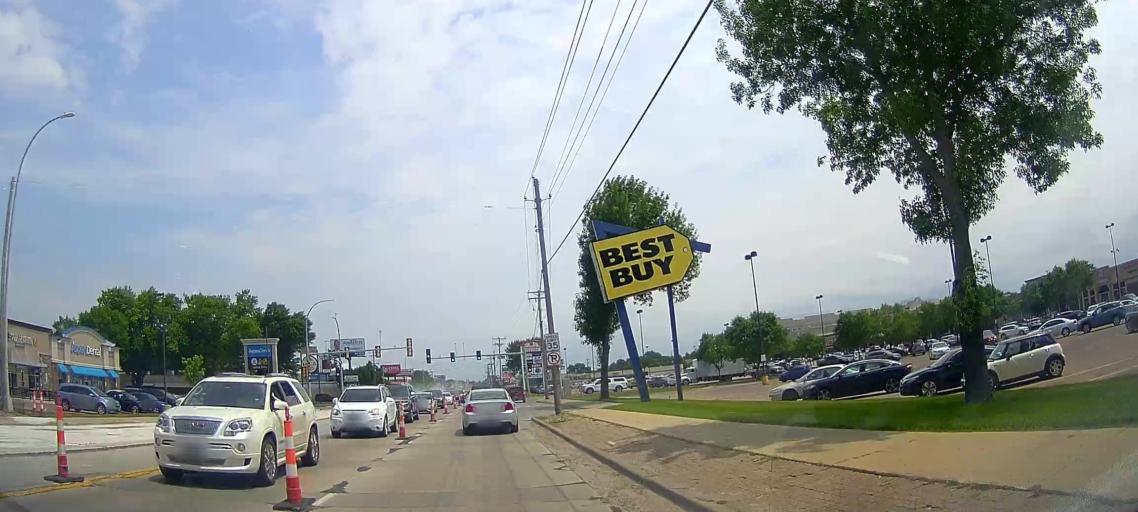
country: US
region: South Dakota
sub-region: Minnehaha County
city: Sioux Falls
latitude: 43.5148
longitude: -96.7558
